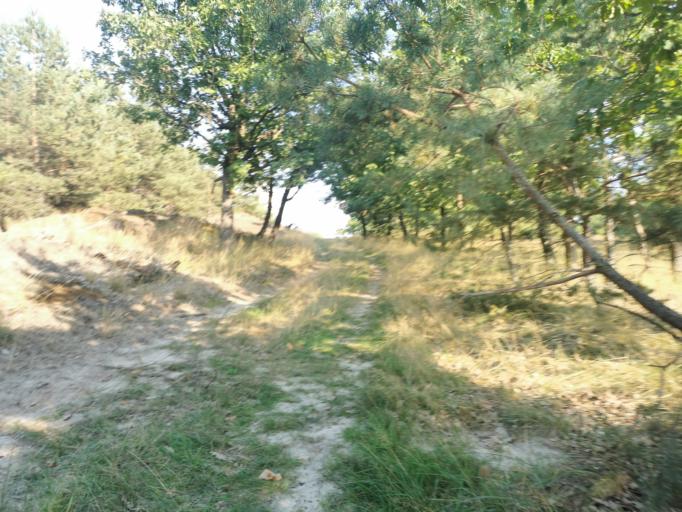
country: SK
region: Trnavsky
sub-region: Okres Senica
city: Senica
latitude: 48.6430
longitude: 17.2953
